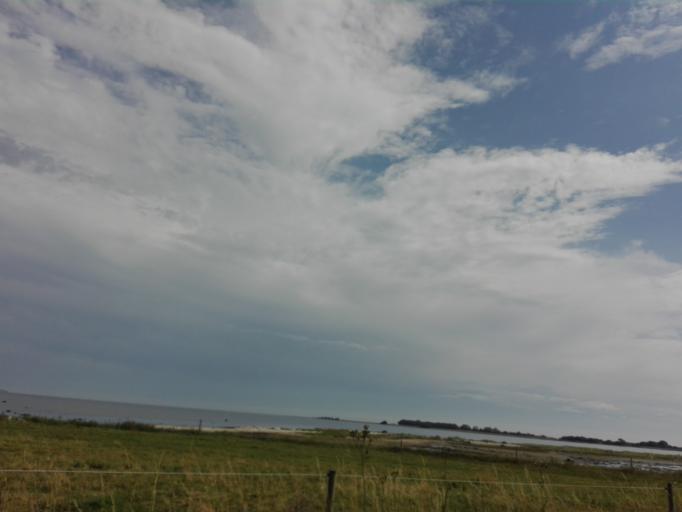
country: DK
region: Central Jutland
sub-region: Hedensted Kommune
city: Juelsminde
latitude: 55.8449
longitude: 10.0478
